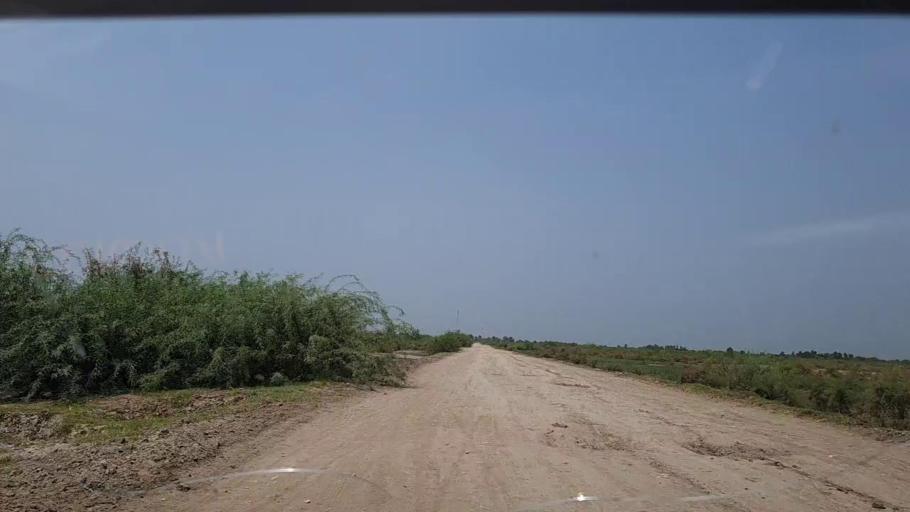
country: PK
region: Sindh
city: Adilpur
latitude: 27.9087
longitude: 69.2186
